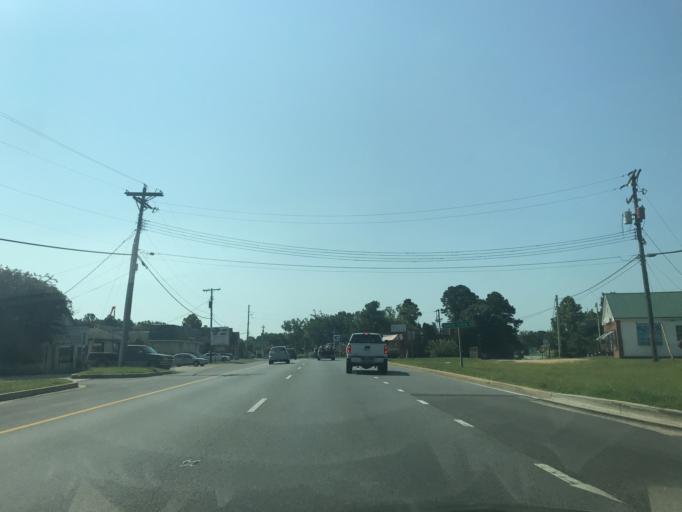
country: US
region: Maryland
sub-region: Saint Mary's County
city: Charlotte Hall
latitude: 38.4730
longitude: -76.7749
